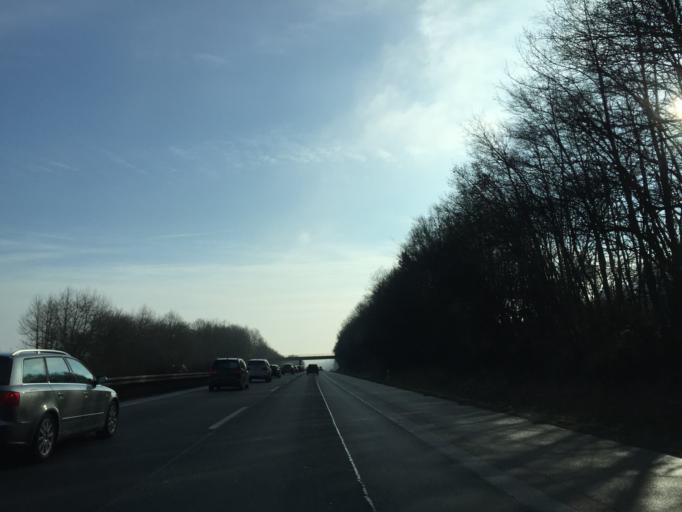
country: DE
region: Bavaria
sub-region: Regierungsbezirk Unterfranken
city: Geiselwind
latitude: 49.7679
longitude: 10.4971
